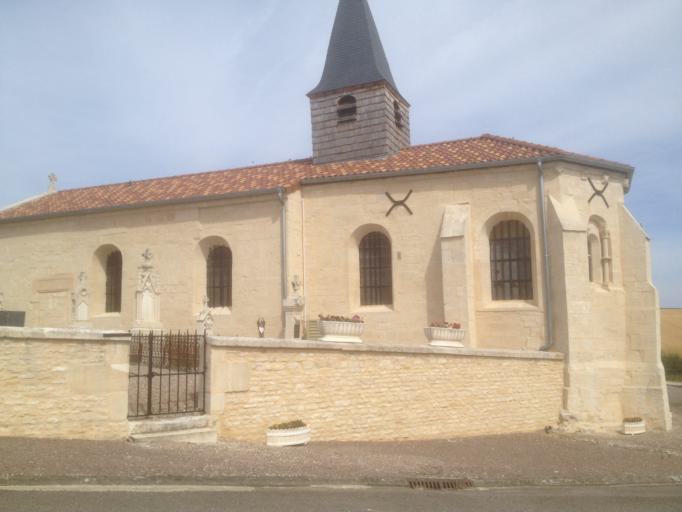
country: FR
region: Champagne-Ardenne
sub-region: Departement de la Haute-Marne
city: Joinville
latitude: 48.4558
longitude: 5.2869
